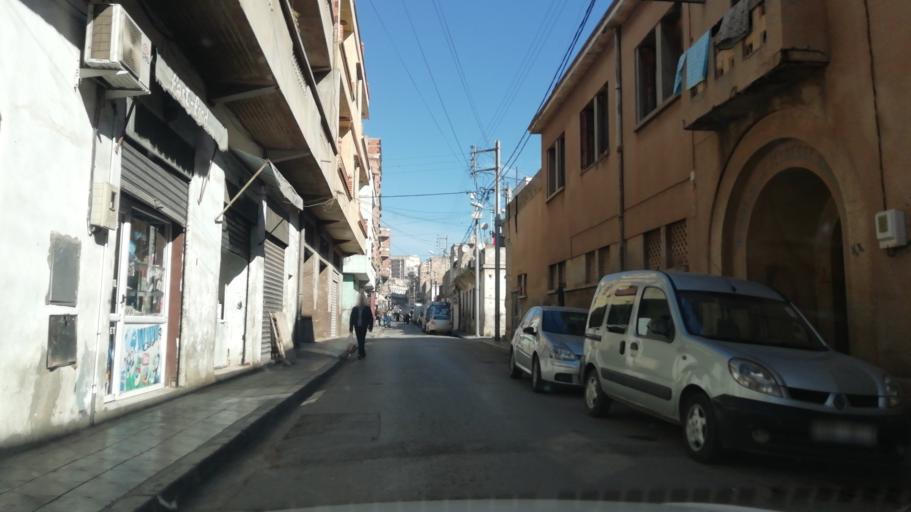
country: DZ
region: Oran
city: Oran
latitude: 35.6969
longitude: -0.6237
